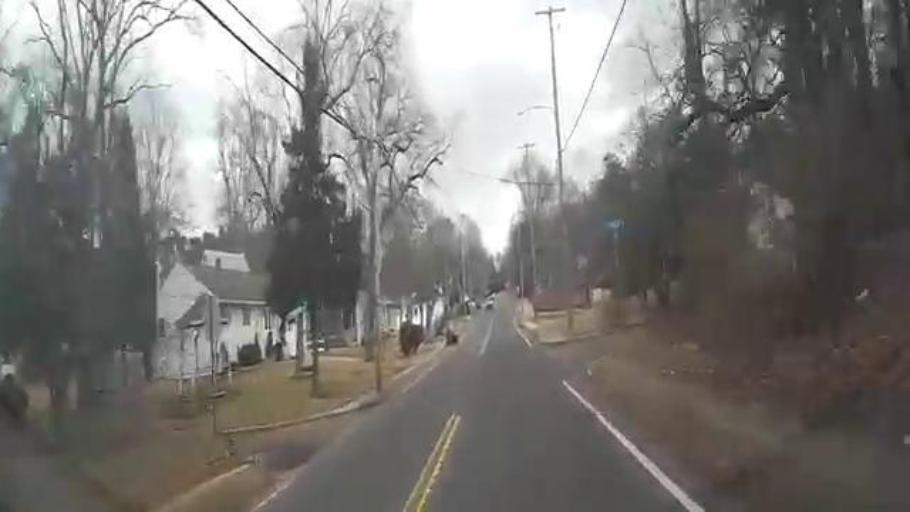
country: US
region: New Jersey
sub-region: Camden County
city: Clementon
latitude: 39.8008
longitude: -74.9713
